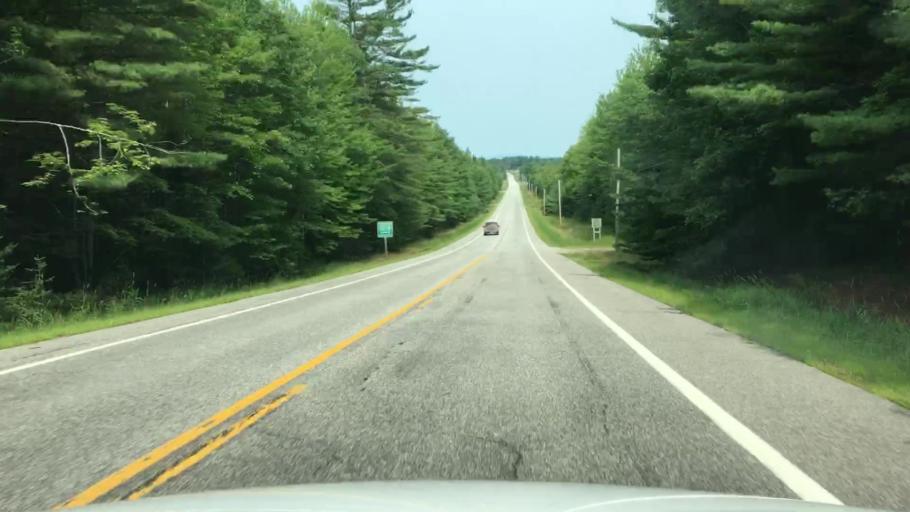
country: US
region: Maine
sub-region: Kennebec County
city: Wayne
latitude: 44.3828
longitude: -70.1050
